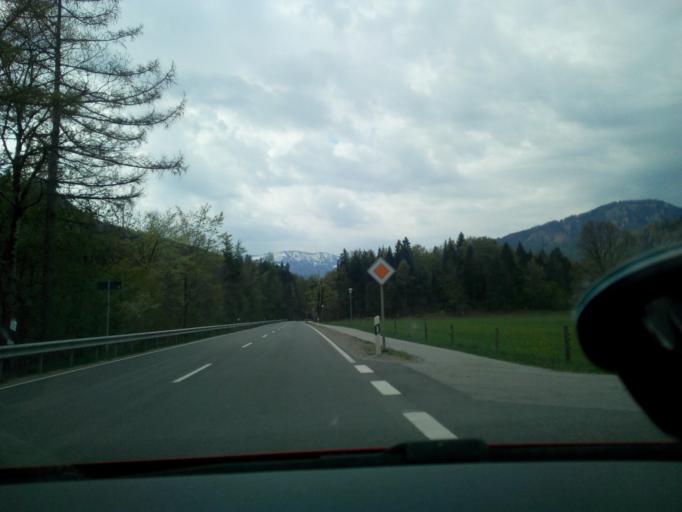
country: DE
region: Bavaria
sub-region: Upper Bavaria
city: Kreuth
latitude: 47.6595
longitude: 11.7493
